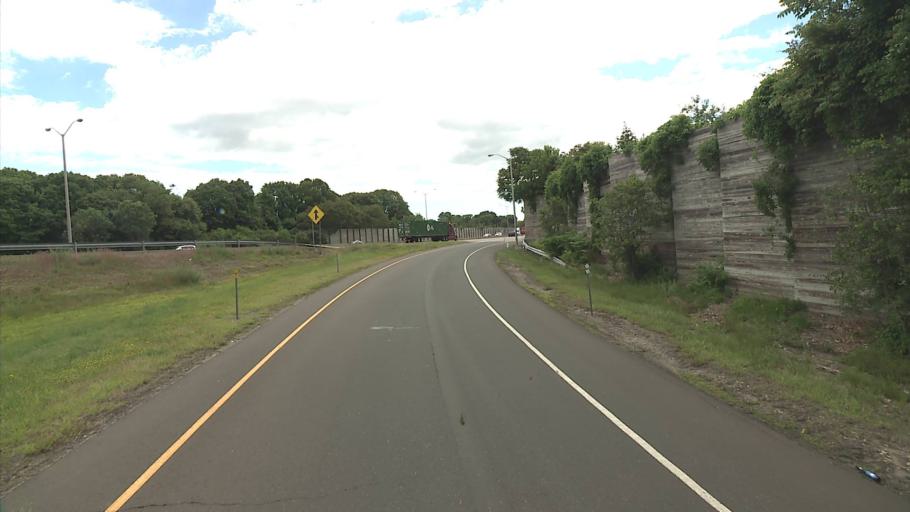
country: US
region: Connecticut
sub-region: Middlesex County
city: Old Saybrook Center
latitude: 41.3160
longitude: -72.3603
